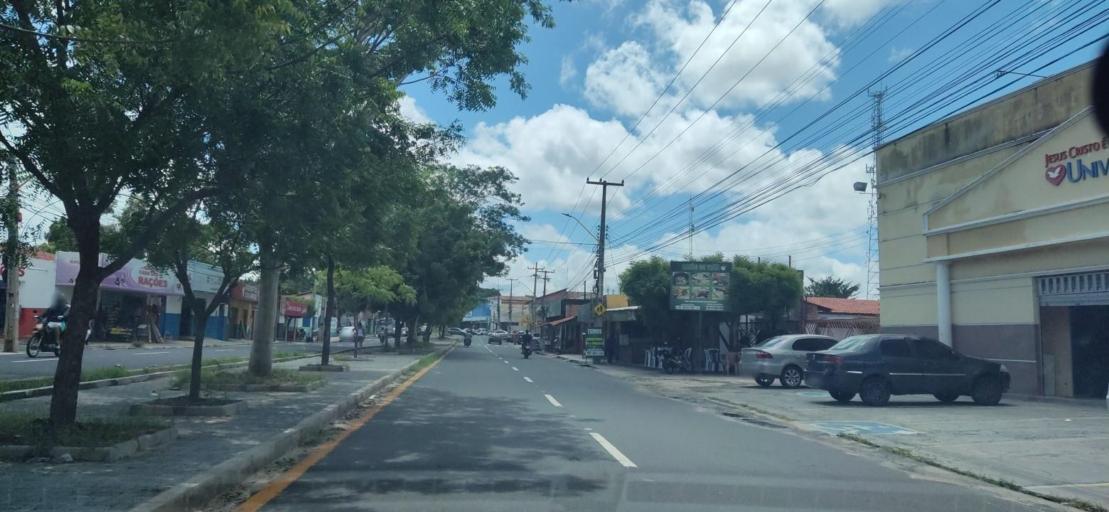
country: BR
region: Piaui
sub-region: Teresina
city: Teresina
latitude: -5.0649
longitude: -42.7621
